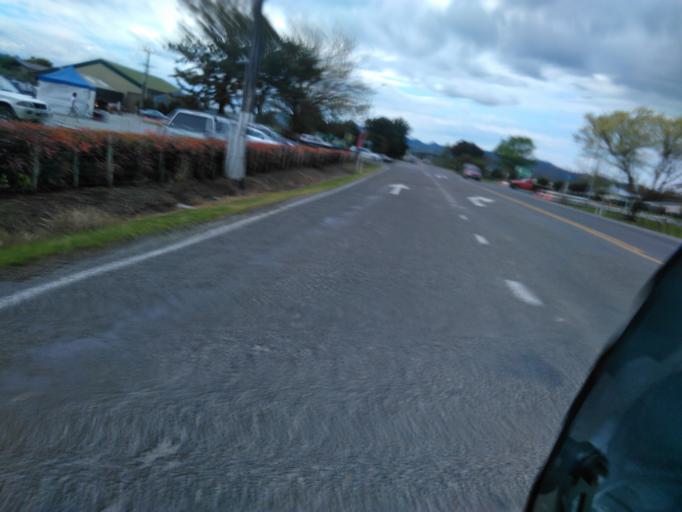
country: NZ
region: Gisborne
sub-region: Gisborne District
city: Gisborne
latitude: -38.6576
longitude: 177.9469
